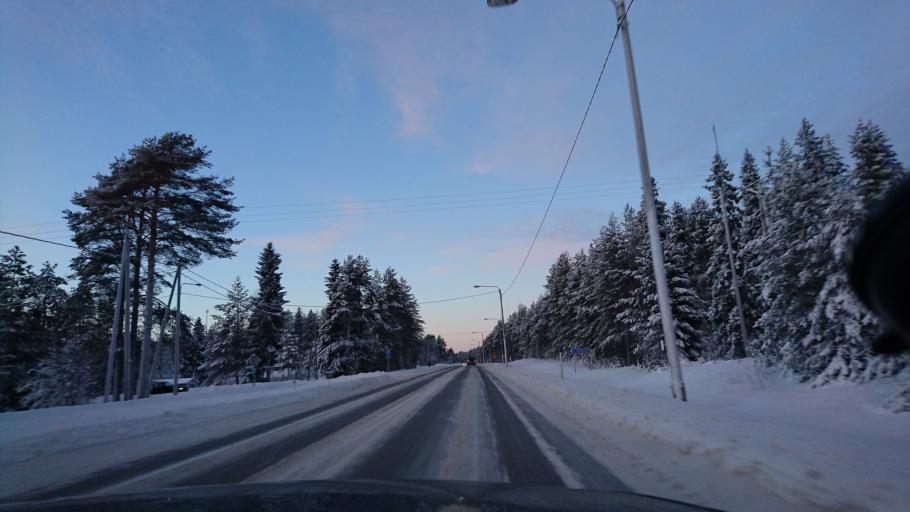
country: FI
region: Lapland
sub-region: Rovaniemi
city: Ranua
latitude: 65.9400
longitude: 26.4821
